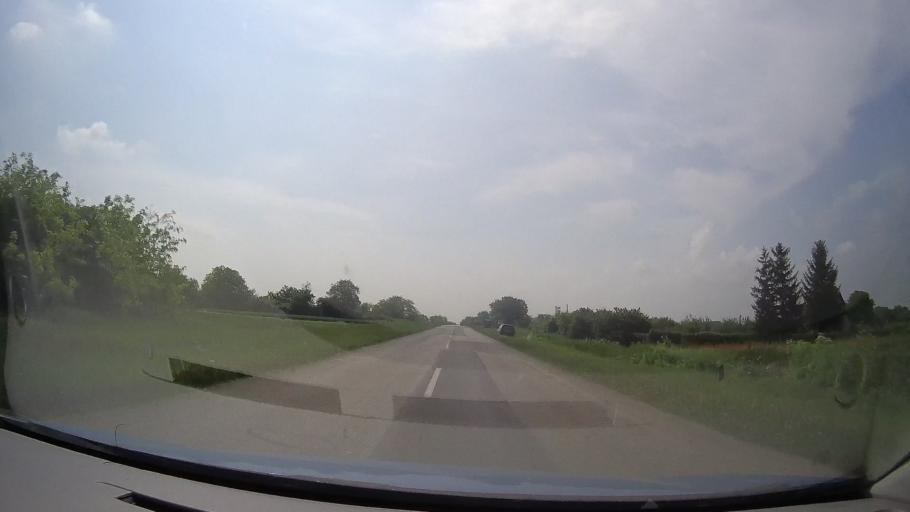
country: RS
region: Autonomna Pokrajina Vojvodina
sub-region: Juznobanatski Okrug
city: Kovacica
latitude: 45.0951
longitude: 20.6299
